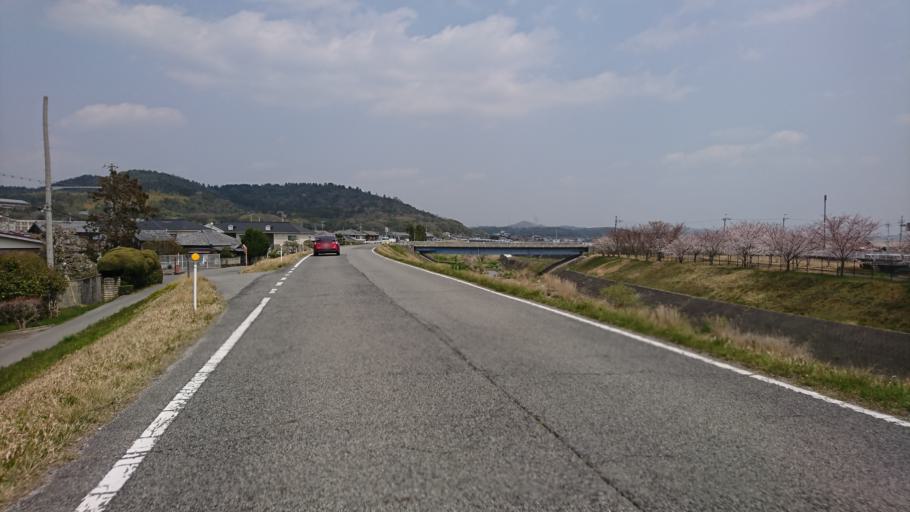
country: JP
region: Hyogo
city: Kakogawacho-honmachi
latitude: 34.7980
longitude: 134.8705
